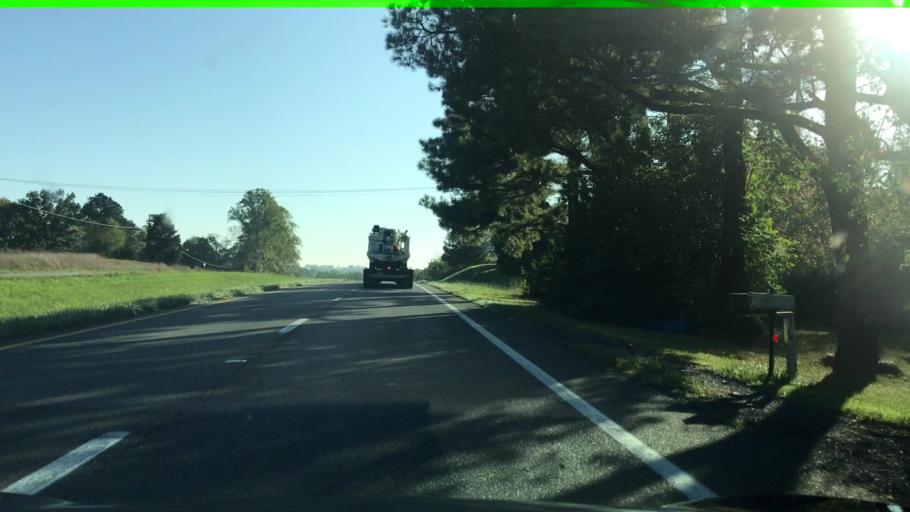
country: US
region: Virginia
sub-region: City of Bedford
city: Bedford
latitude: 37.3140
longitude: -79.4573
